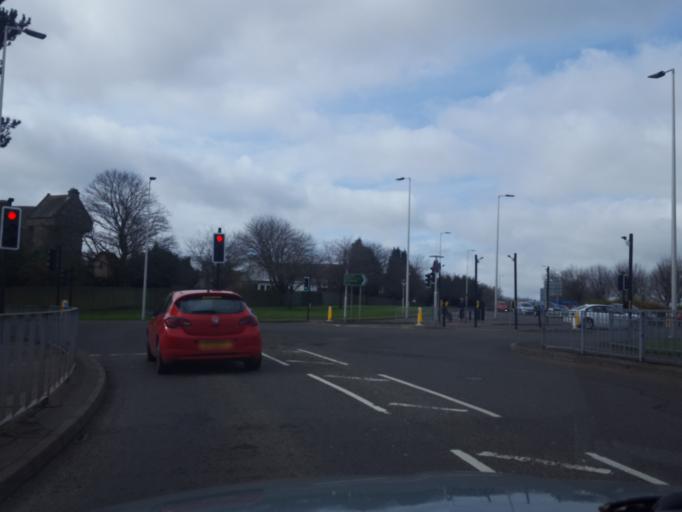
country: GB
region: Scotland
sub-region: Fife
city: Tayport
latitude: 56.4773
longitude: -2.8890
